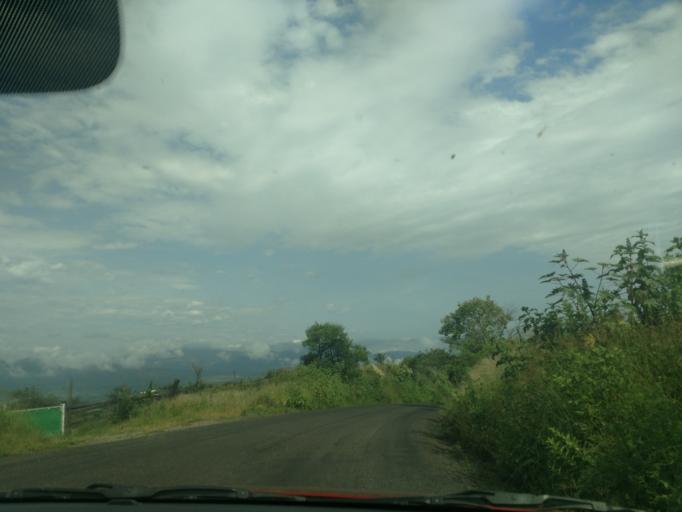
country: MX
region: Jalisco
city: El Salto
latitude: 20.4335
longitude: -104.4525
